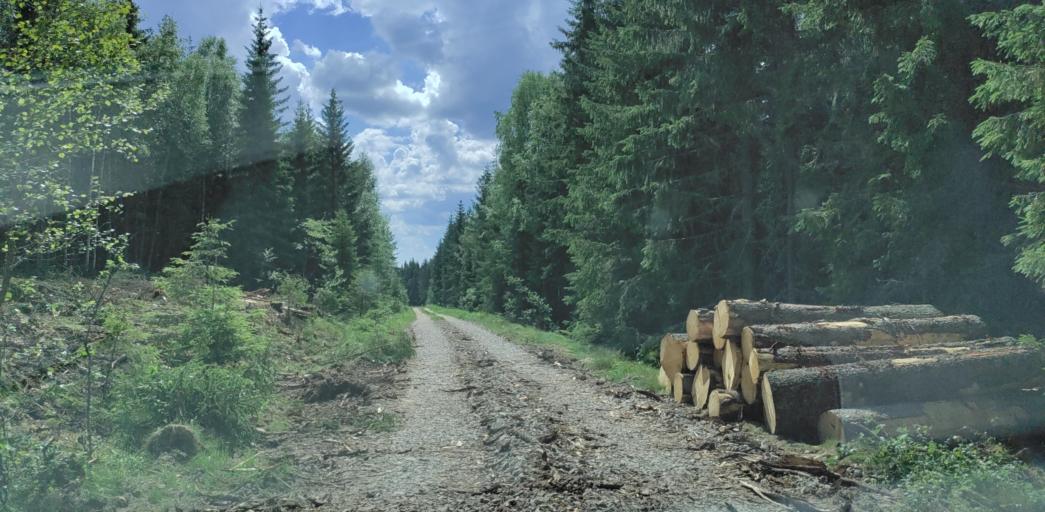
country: SE
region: Vaermland
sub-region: Hagfors Kommun
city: Ekshaerad
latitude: 60.0670
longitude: 13.3414
